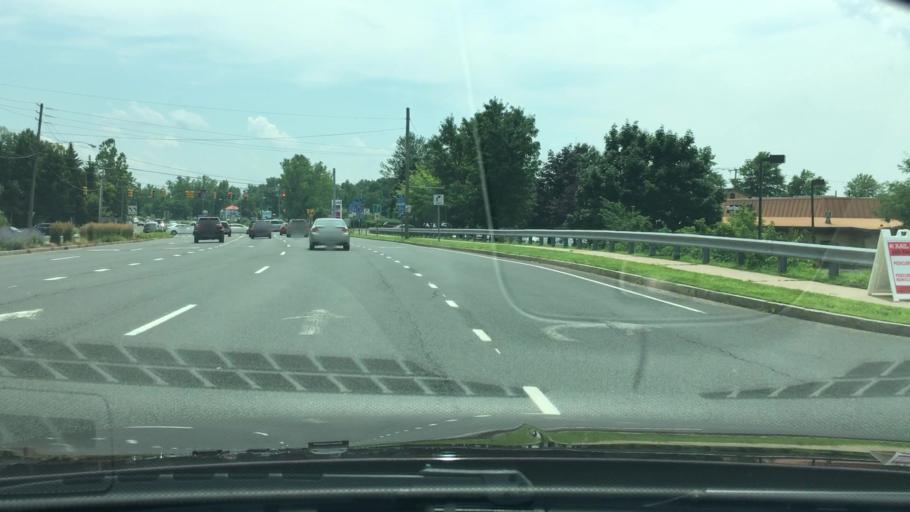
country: US
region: Connecticut
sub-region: Hartford County
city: Manchester
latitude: 41.8074
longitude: -72.5554
